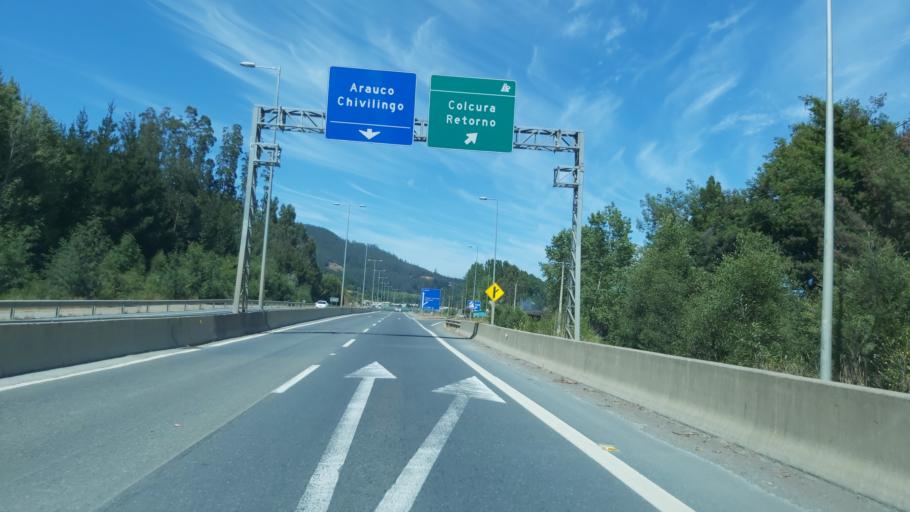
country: CL
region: Biobio
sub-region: Provincia de Concepcion
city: Lota
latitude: -37.1054
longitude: -73.1393
